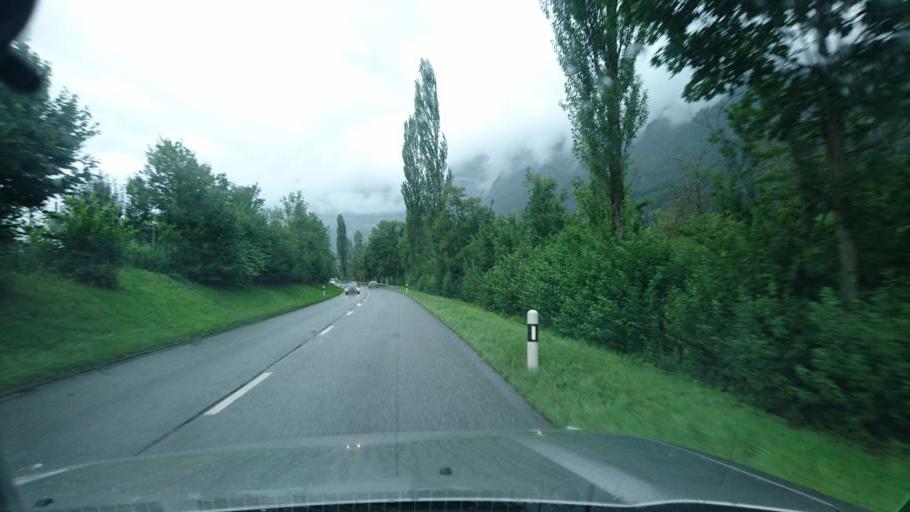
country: CH
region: Saint Gallen
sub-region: Wahlkreis Sarganserland
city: Flums
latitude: 47.1133
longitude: 9.3378
